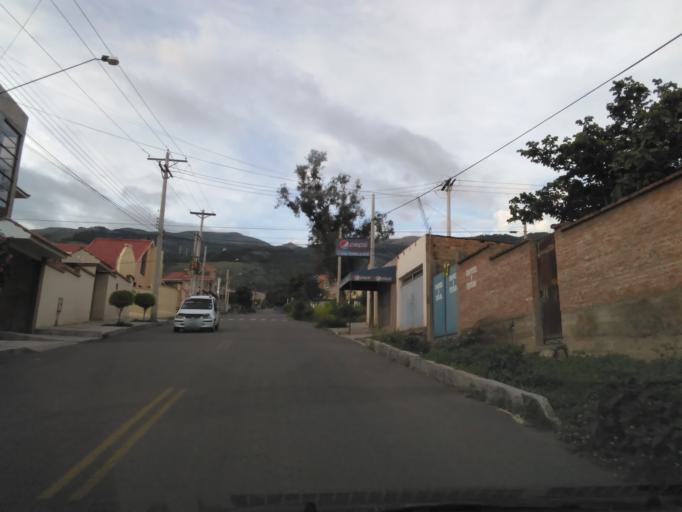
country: BO
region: Cochabamba
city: Cochabamba
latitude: -17.3591
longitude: -66.1559
